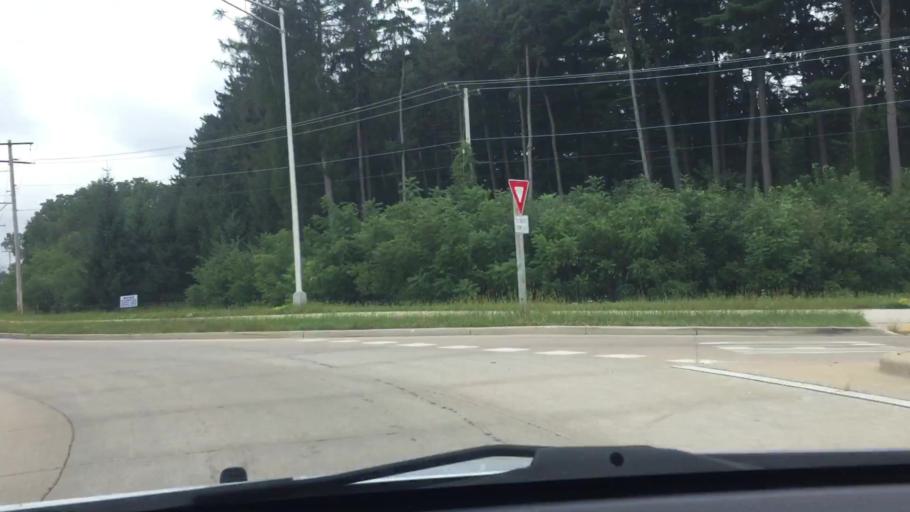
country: US
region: Wisconsin
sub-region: Waukesha County
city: Delafield
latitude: 43.0592
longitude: -88.4426
